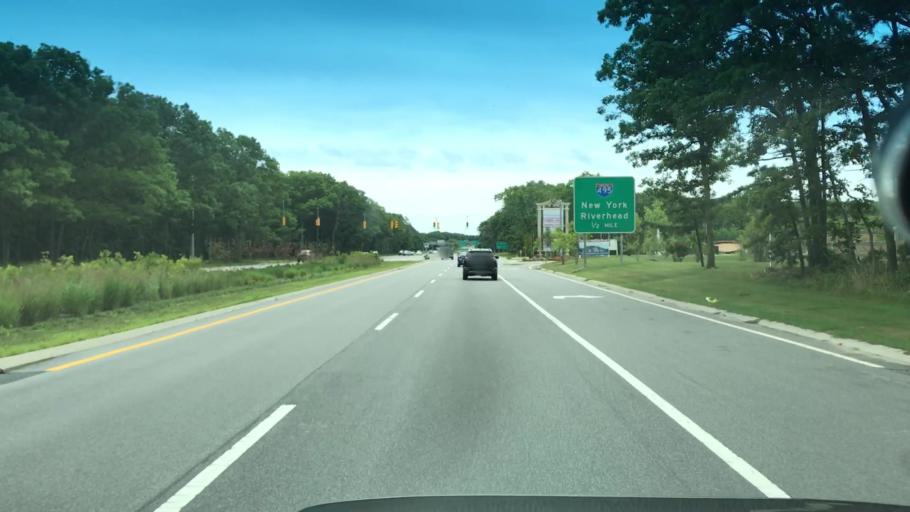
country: US
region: New York
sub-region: Suffolk County
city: Yaphank
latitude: 40.8500
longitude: -72.8959
